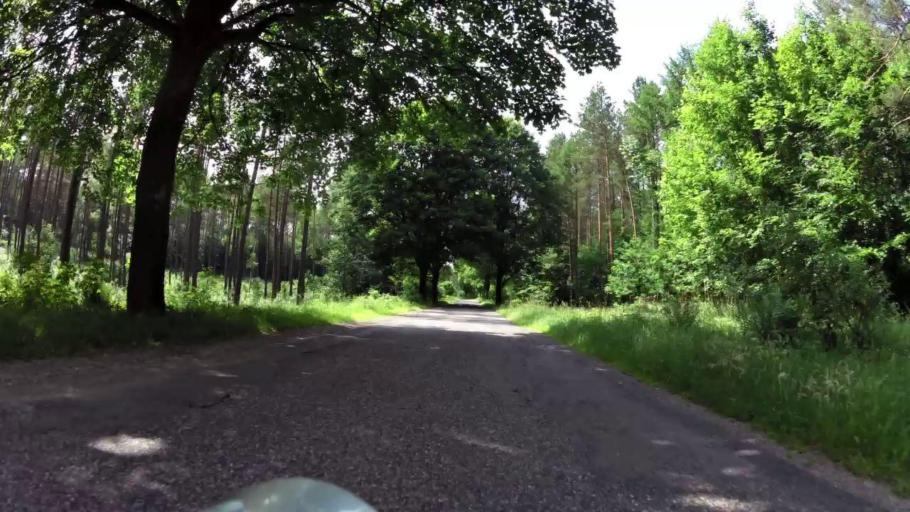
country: PL
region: West Pomeranian Voivodeship
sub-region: Powiat szczecinecki
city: Bialy Bor
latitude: 53.9559
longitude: 16.7511
